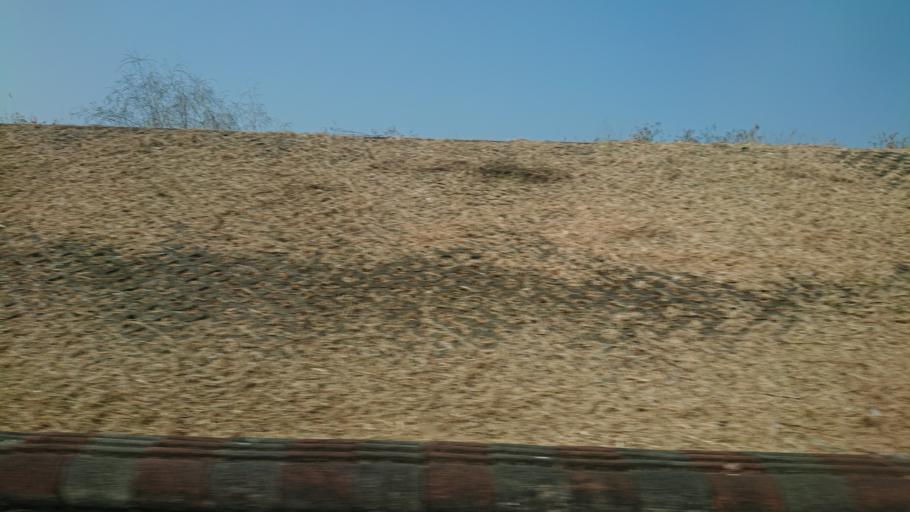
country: TW
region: Taiwan
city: Lugu
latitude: 23.7487
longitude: 120.6587
